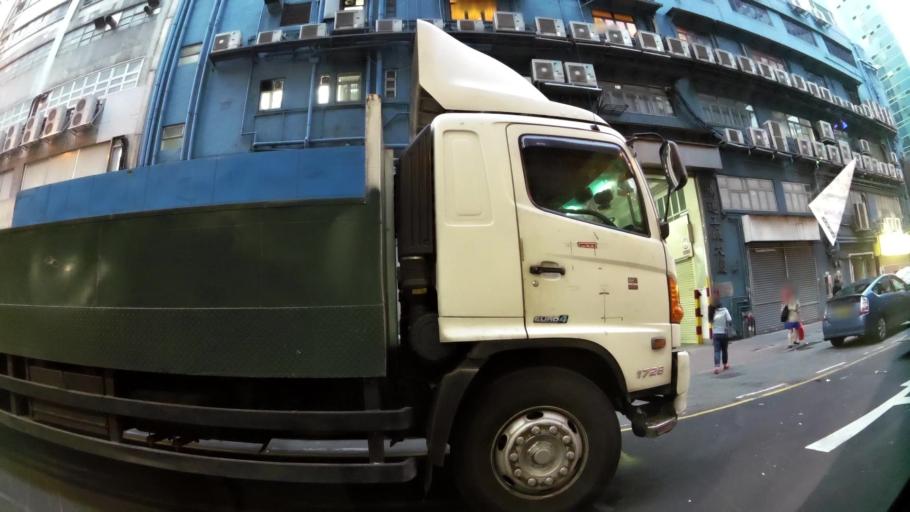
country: HK
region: Kowloon City
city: Kowloon
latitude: 22.3101
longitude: 114.2230
